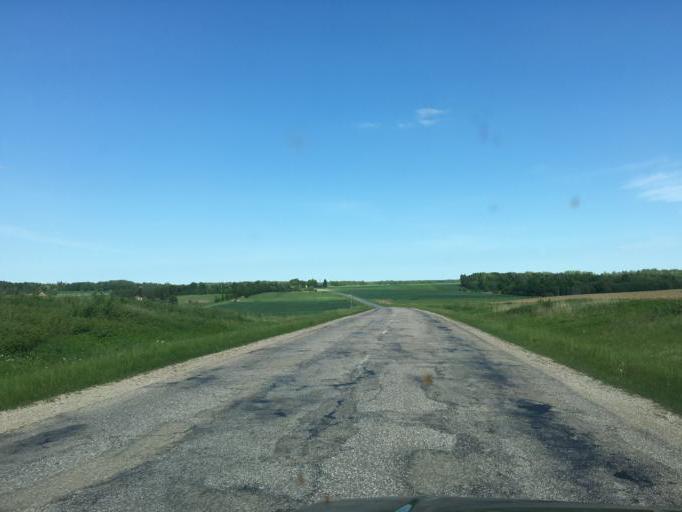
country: LV
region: Talsu Rajons
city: Valdemarpils
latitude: 57.3635
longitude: 22.4898
